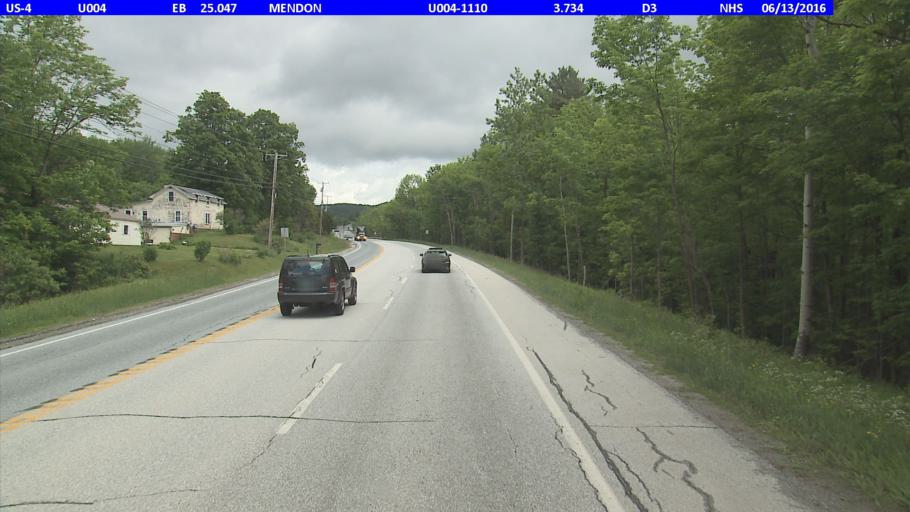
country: US
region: Vermont
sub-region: Rutland County
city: Rutland
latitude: 43.6554
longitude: -72.8833
